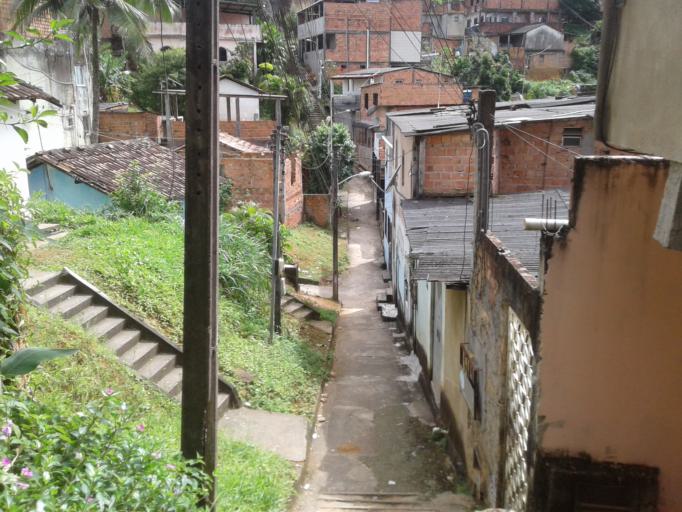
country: BR
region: Bahia
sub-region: Salvador
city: Salvador
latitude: -12.9096
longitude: -38.4747
